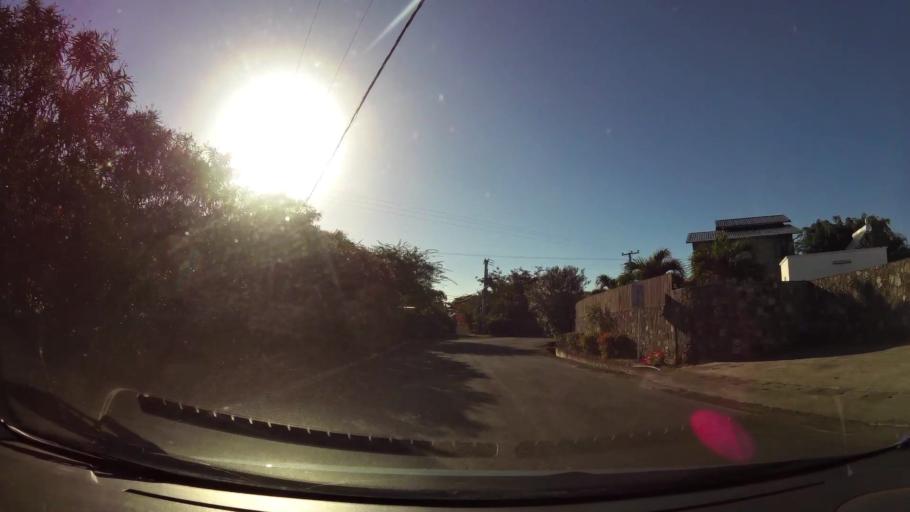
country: MU
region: Black River
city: Tamarin
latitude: -20.3352
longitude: 57.3791
